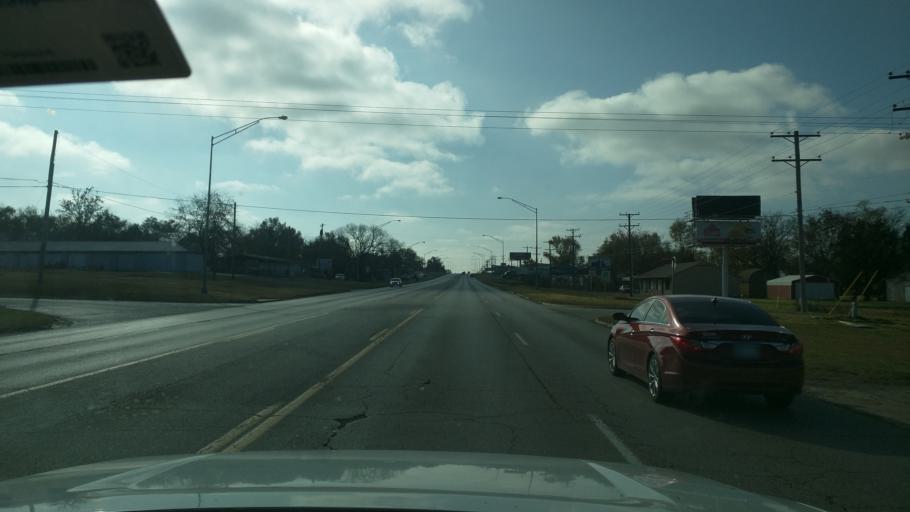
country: US
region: Oklahoma
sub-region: Washington County
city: Dewey
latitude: 36.7719
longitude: -95.9355
